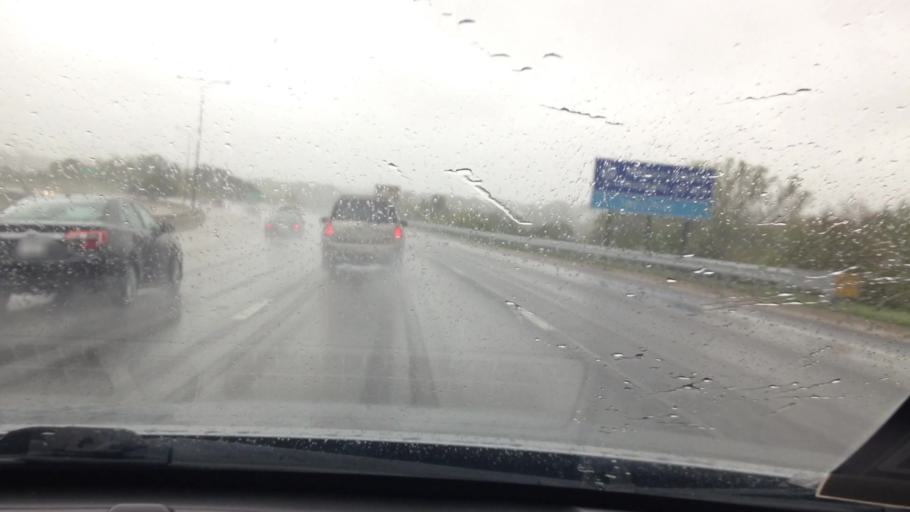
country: US
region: Kansas
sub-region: Johnson County
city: Westwood
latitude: 39.0345
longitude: -94.5533
